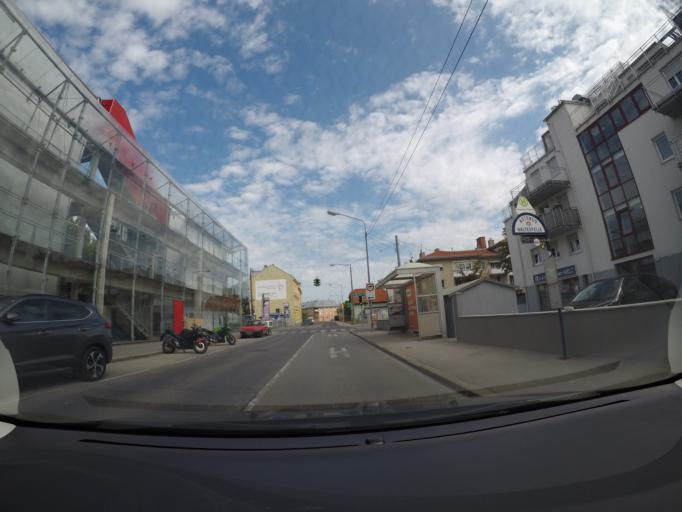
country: AT
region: Lower Austria
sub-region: Politischer Bezirk Modling
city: Brunn am Gebirge
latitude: 48.1434
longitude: 16.2979
